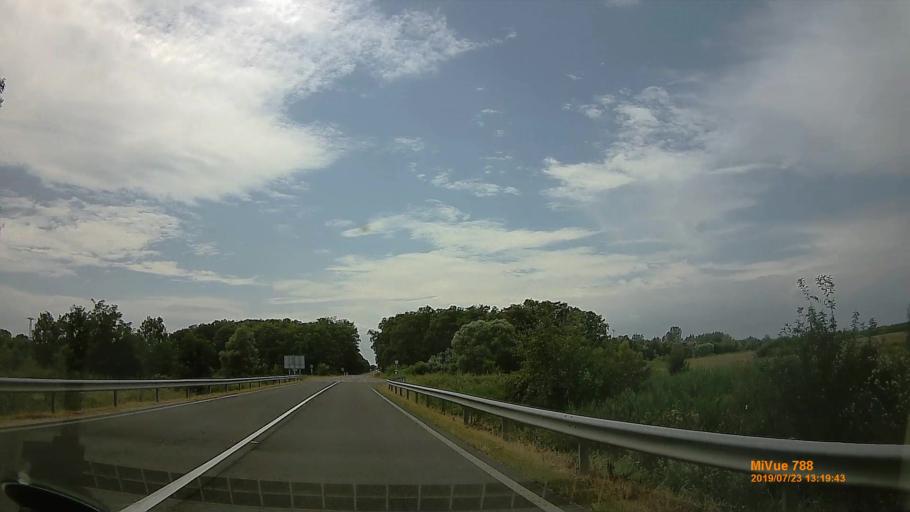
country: HU
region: Hajdu-Bihar
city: Polgar
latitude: 47.8720
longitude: 21.1365
